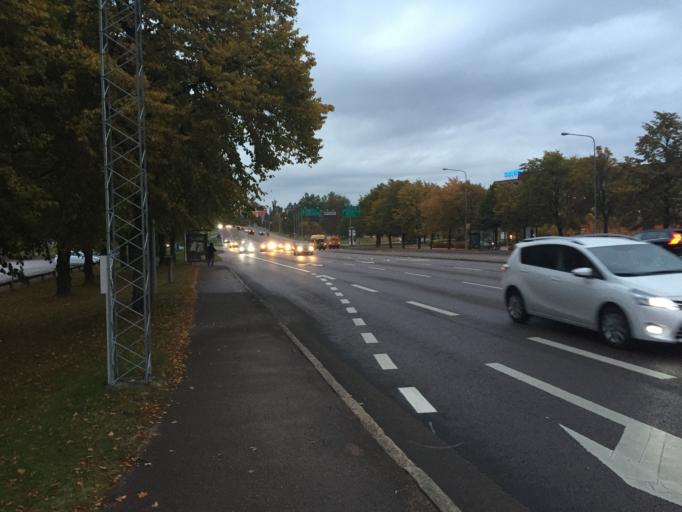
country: SE
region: Vaermland
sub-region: Karlstads Kommun
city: Karlstad
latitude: 59.3820
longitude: 13.4883
